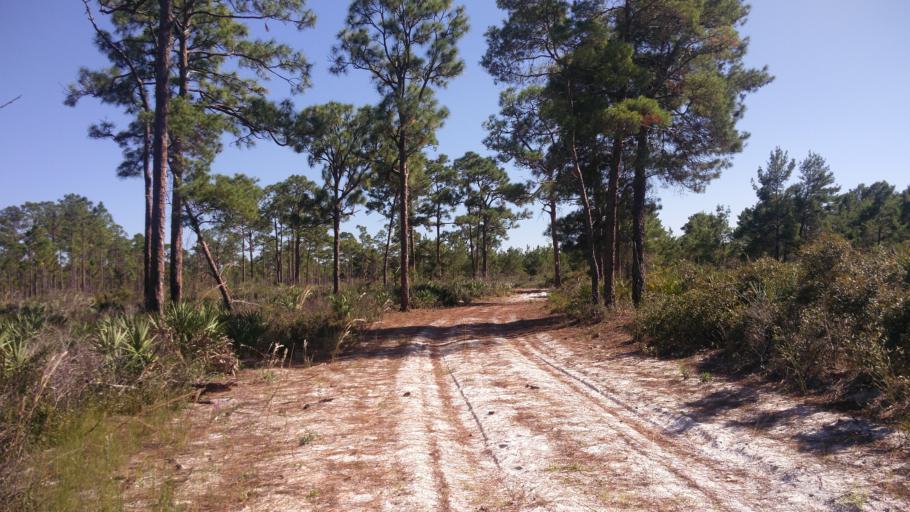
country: US
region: Florida
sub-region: Martin County
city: Hobe Sound
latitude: 27.0261
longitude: -80.1318
